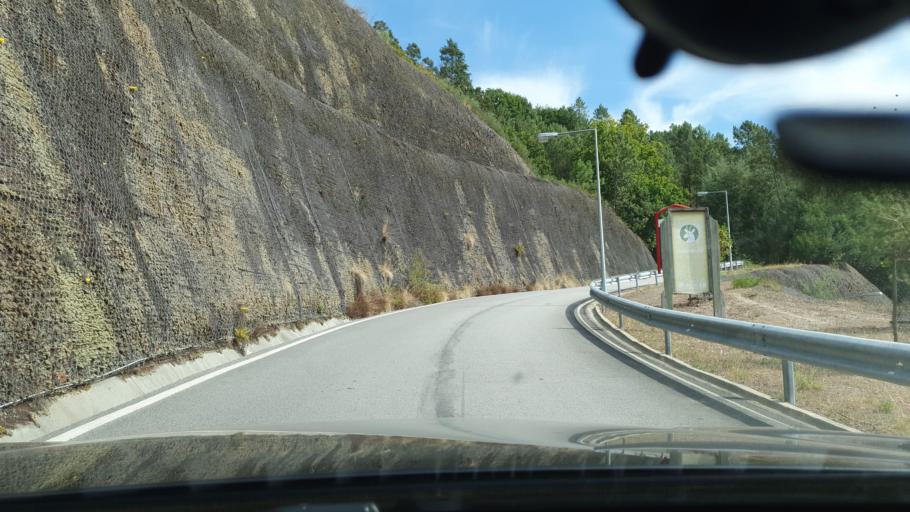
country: PT
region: Braga
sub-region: Vieira do Minho
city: Vieira do Minho
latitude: 41.6930
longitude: -8.0921
